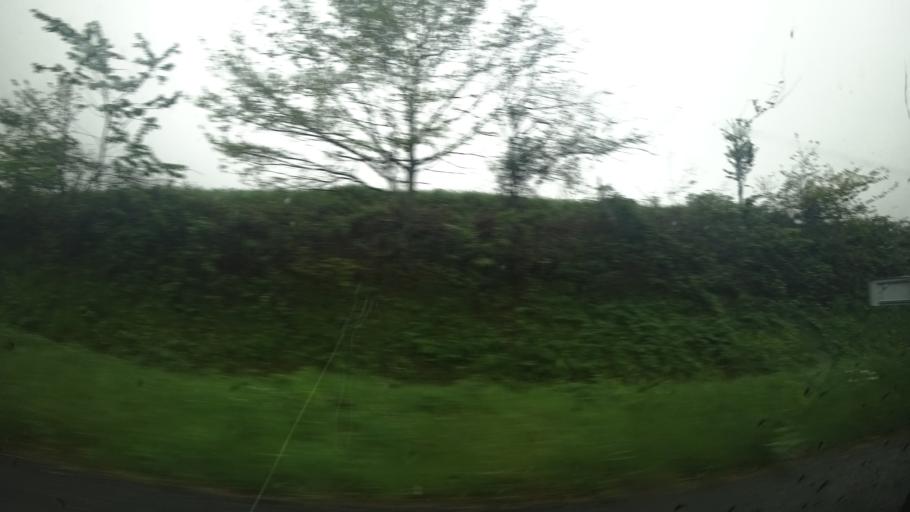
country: FR
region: Midi-Pyrenees
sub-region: Departement de l'Aveyron
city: Laissac
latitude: 44.3242
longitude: 2.7888
